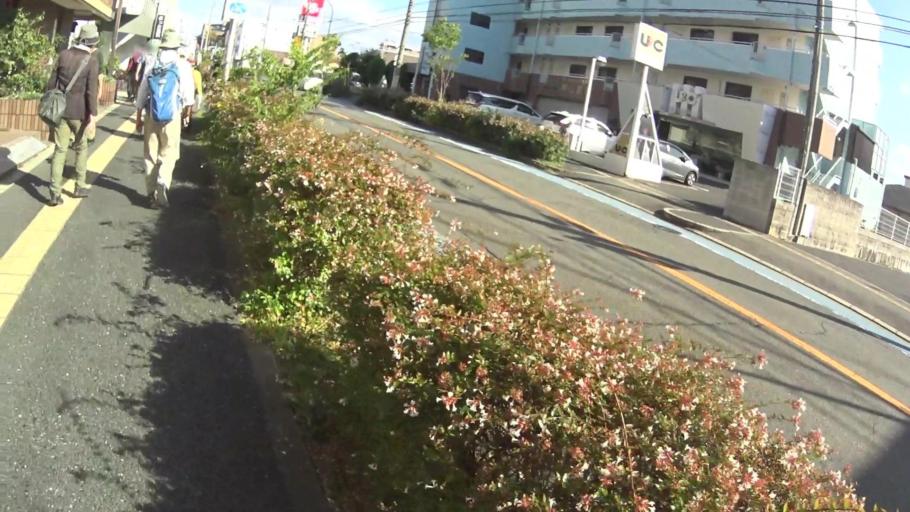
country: JP
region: Ehime
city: Kihoku-cho
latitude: 33.3944
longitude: 132.8530
